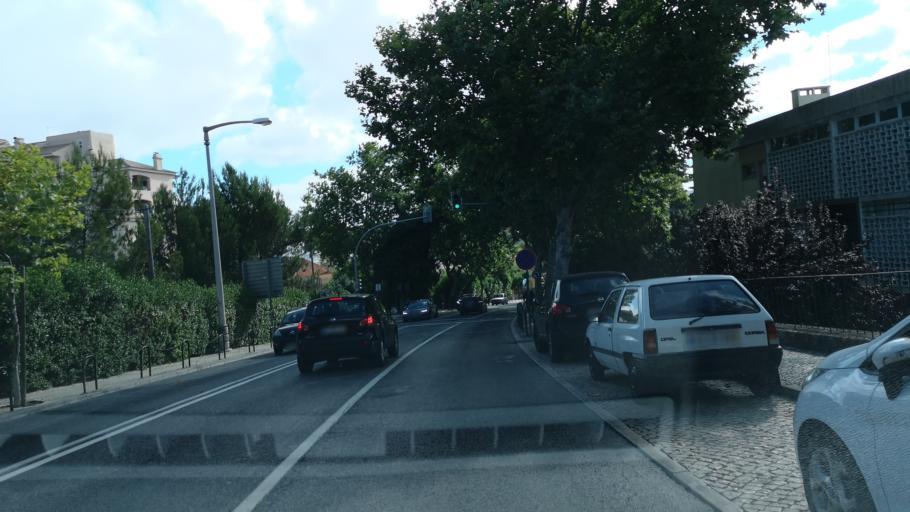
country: PT
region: Lisbon
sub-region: Cascais
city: Cascais
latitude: 38.7009
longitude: -9.4247
